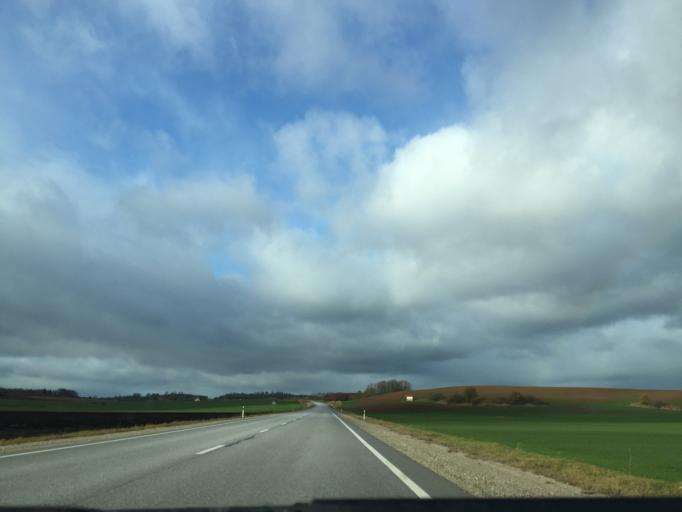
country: LV
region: Tukuma Rajons
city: Tukums
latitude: 56.9668
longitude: 23.0656
